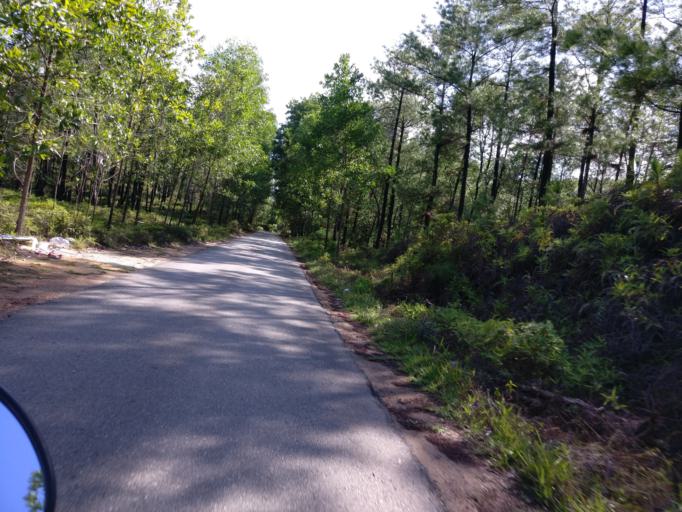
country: VN
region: Thua Thien-Hue
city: Hue
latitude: 16.4076
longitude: 107.5933
